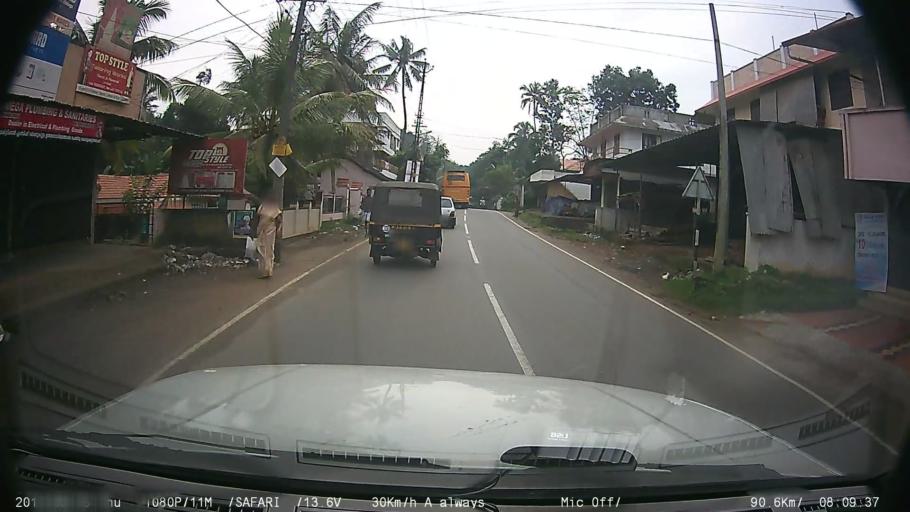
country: IN
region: Kerala
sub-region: Kottayam
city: Kottayam
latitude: 9.6013
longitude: 76.5869
